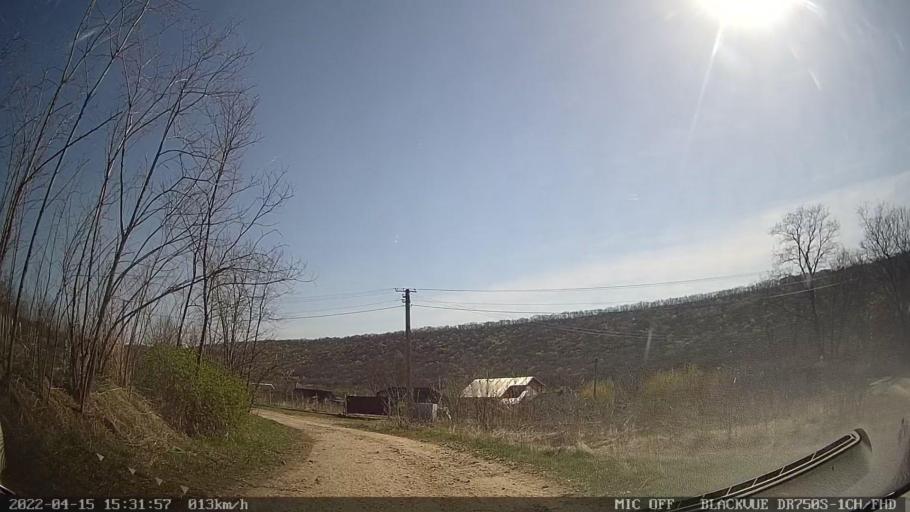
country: MD
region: Raionul Ocnita
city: Otaci
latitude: 48.3516
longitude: 27.9193
